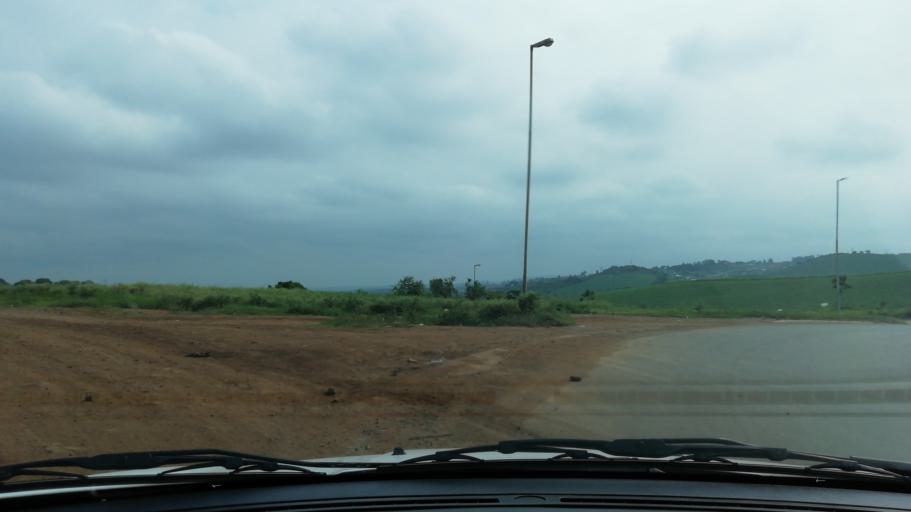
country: ZA
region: KwaZulu-Natal
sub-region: uThungulu District Municipality
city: Empangeni
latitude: -28.7440
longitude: 31.8821
